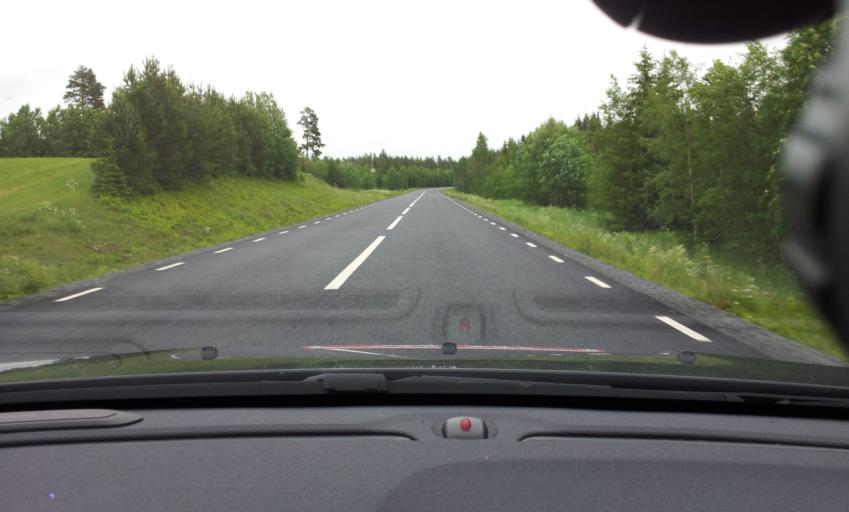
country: SE
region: Jaemtland
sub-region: OEstersunds Kommun
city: Lit
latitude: 63.6725
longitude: 15.1161
